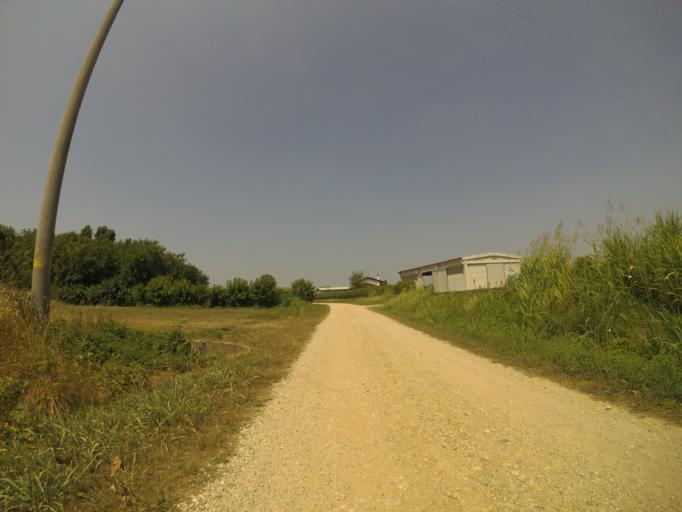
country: IT
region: Friuli Venezia Giulia
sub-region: Provincia di Udine
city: Talmassons
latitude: 45.9226
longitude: 13.1226
